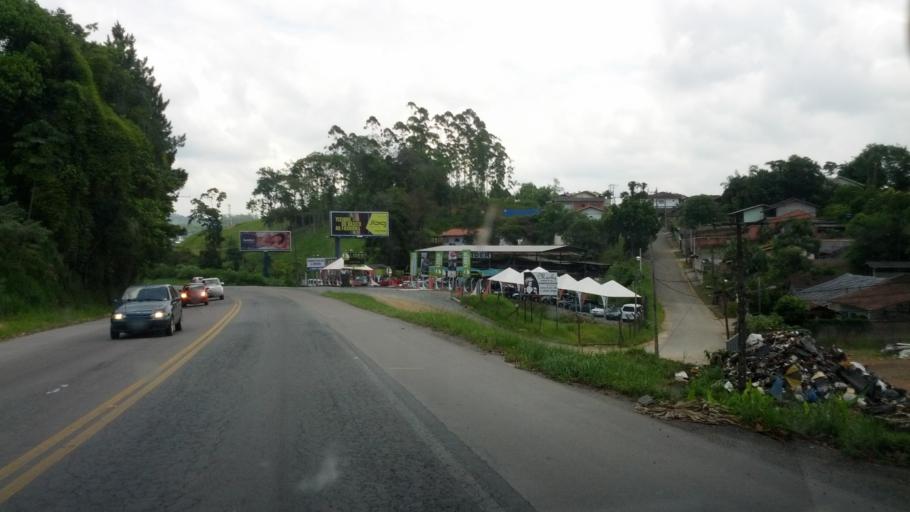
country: BR
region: Santa Catarina
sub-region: Blumenau
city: Blumenau
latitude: -26.8786
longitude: -49.1339
